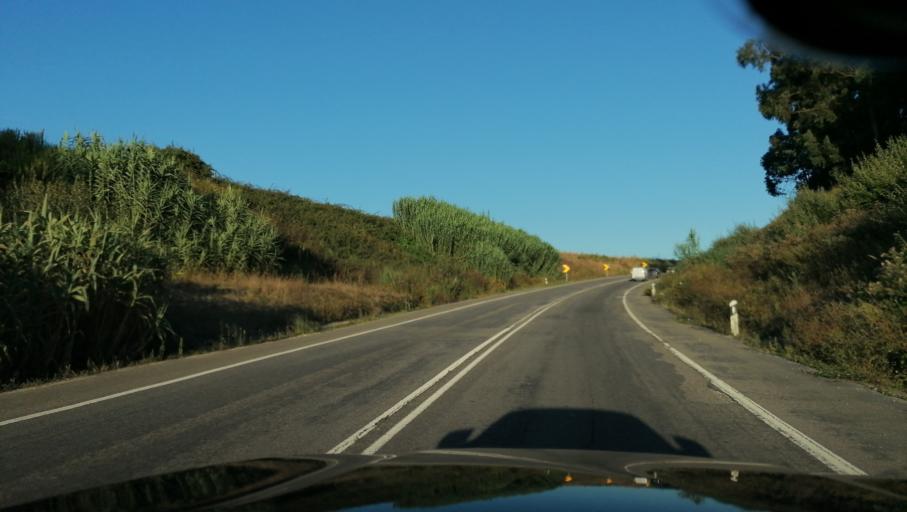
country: PT
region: Aveiro
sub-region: Aveiro
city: Aradas
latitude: 40.6107
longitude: -8.6277
